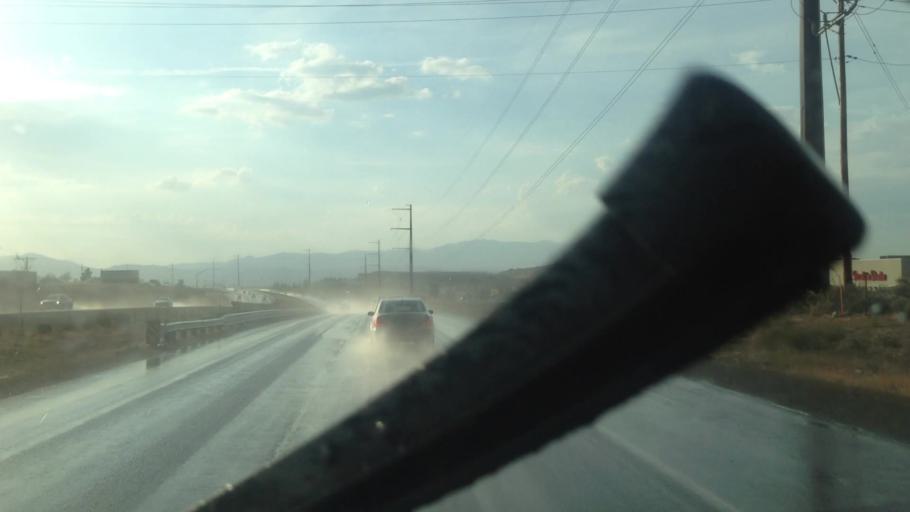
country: US
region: Nevada
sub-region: Washoe County
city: Golden Valley
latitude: 39.6062
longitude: -119.8438
